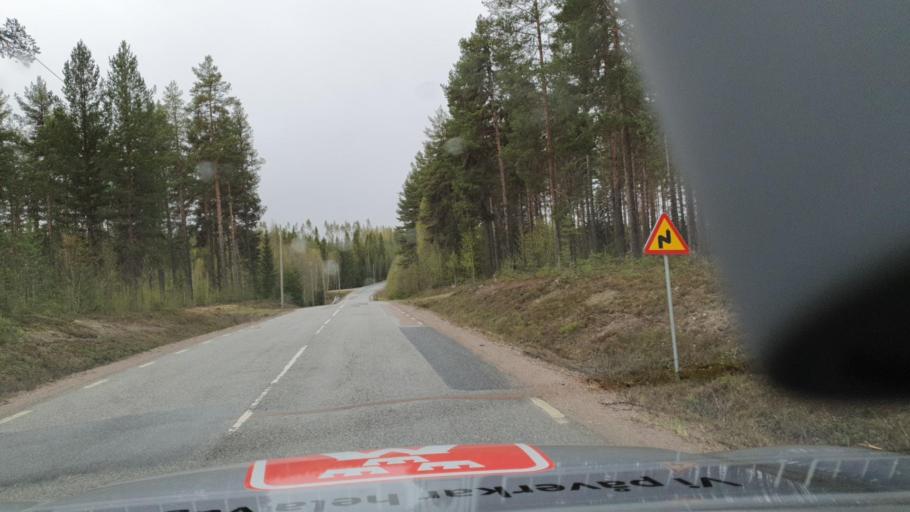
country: SE
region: Vaesterbotten
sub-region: Asele Kommun
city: Asele
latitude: 63.6962
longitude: 17.0346
